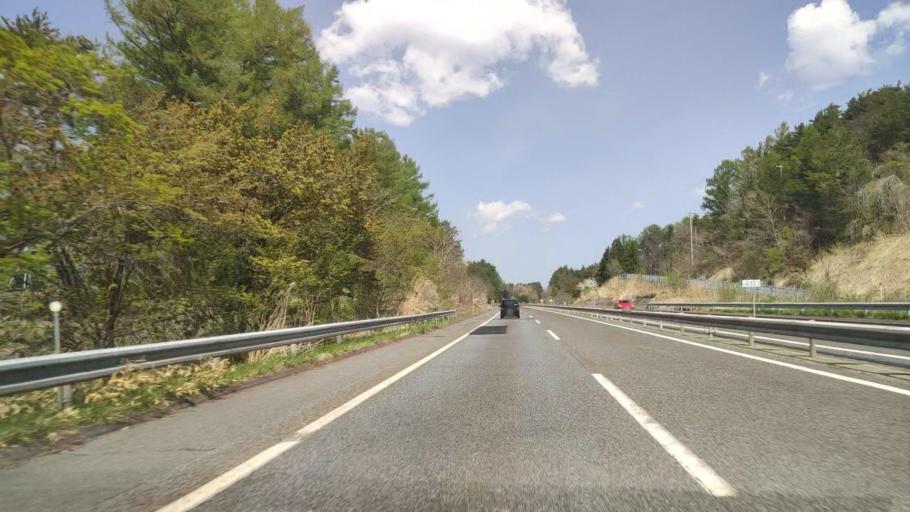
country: JP
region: Aomori
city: Hachinohe
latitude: 40.3408
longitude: 141.4506
